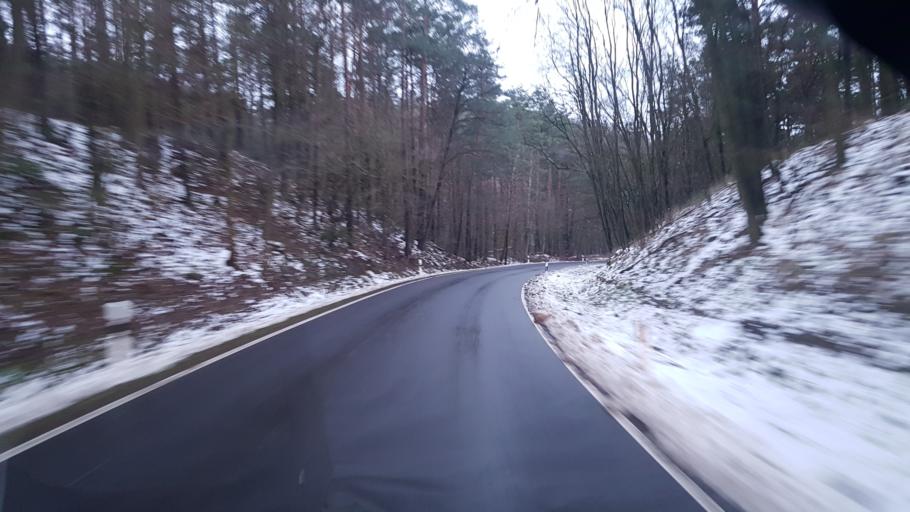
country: DE
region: Brandenburg
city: Brieskow-Finkenheerd
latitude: 52.2798
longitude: 14.5376
